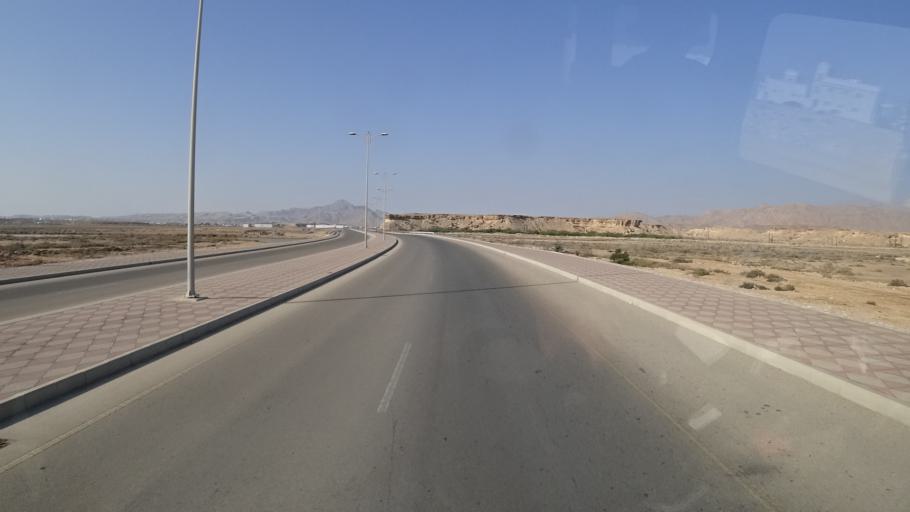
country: OM
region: Ash Sharqiyah
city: Sur
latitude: 22.5981
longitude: 59.4798
